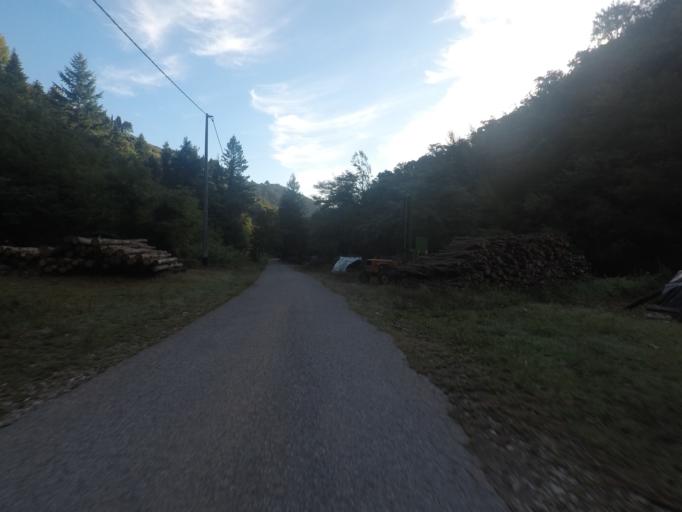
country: IT
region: Tuscany
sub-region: Provincia di Lucca
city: Pescaglia
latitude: 43.9506
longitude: 10.4173
